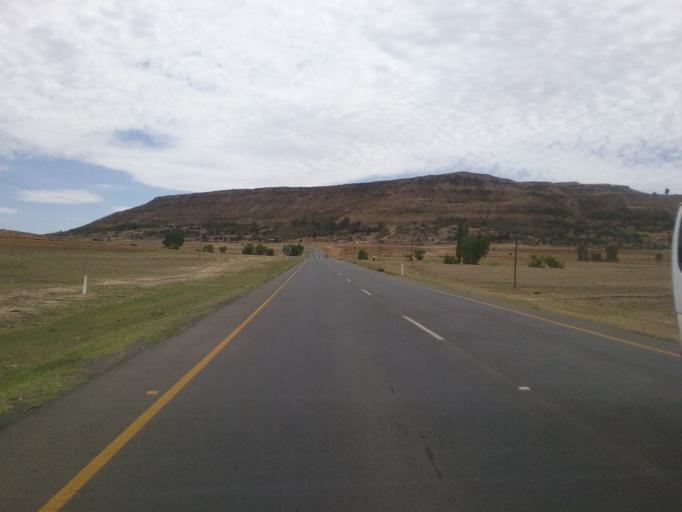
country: LS
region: Maseru
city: Nako
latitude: -29.6138
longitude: 27.4999
